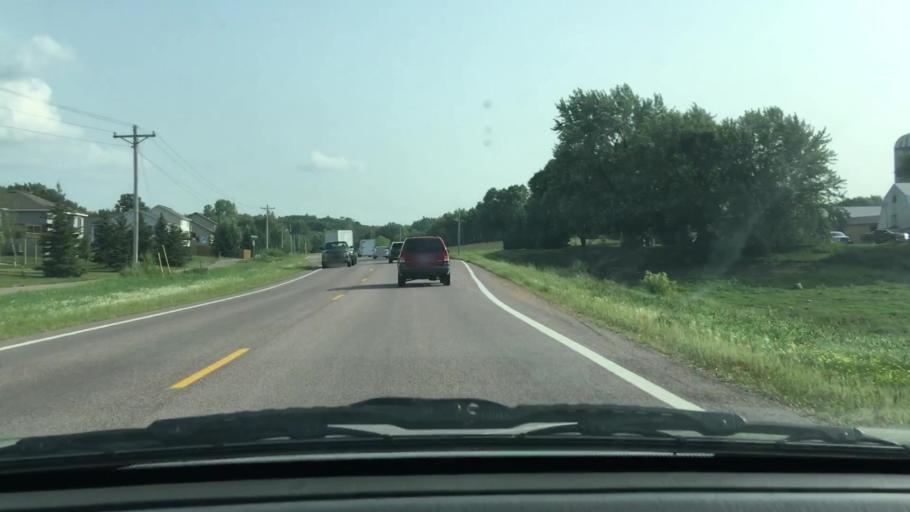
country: US
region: Minnesota
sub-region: Scott County
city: Elko New Market
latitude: 44.5646
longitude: -93.3388
